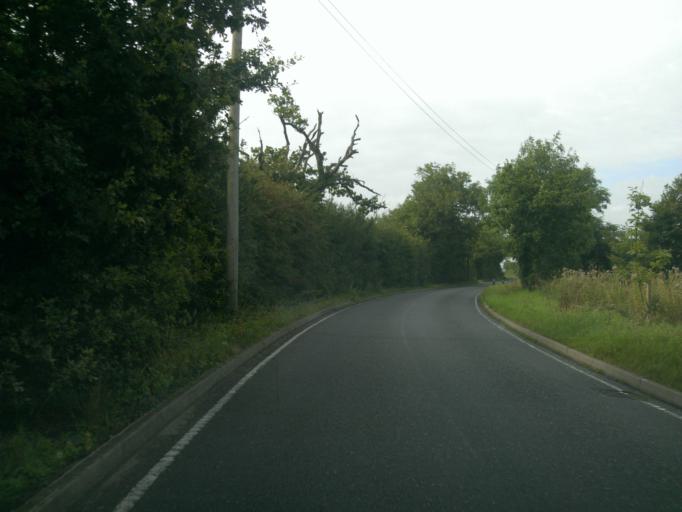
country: GB
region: England
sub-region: Essex
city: Great Bentley
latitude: 51.8310
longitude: 1.0758
